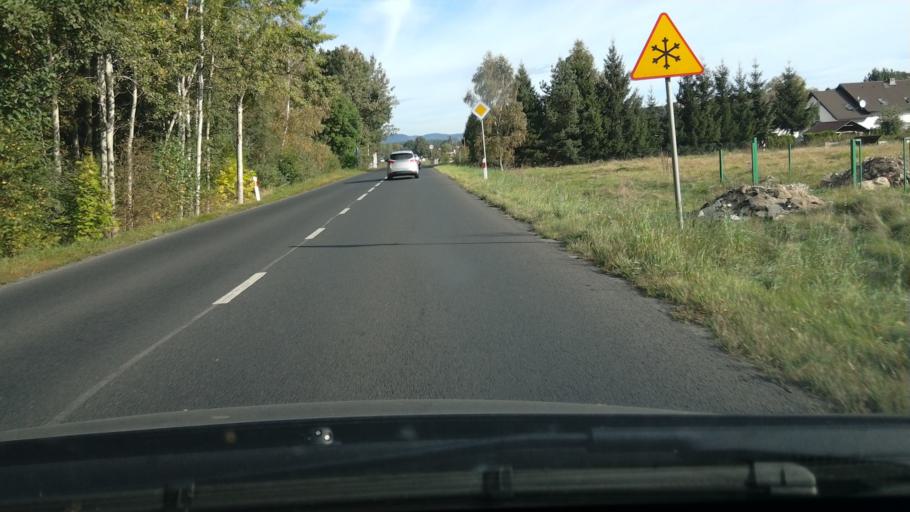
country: PL
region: Lower Silesian Voivodeship
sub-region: Powiat jeleniogorski
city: Myslakowice
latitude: 50.8367
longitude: 15.7740
